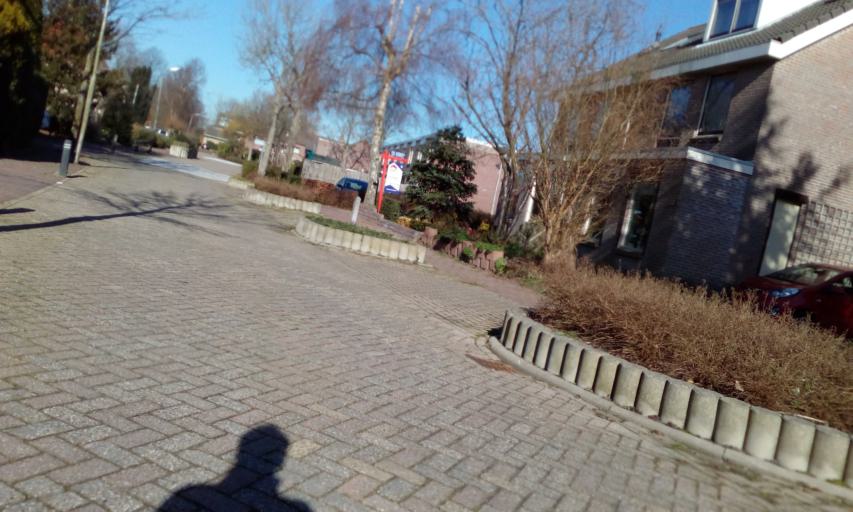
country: NL
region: South Holland
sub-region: Gemeente Lansingerland
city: Bleiswijk
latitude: 52.0065
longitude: 4.5788
